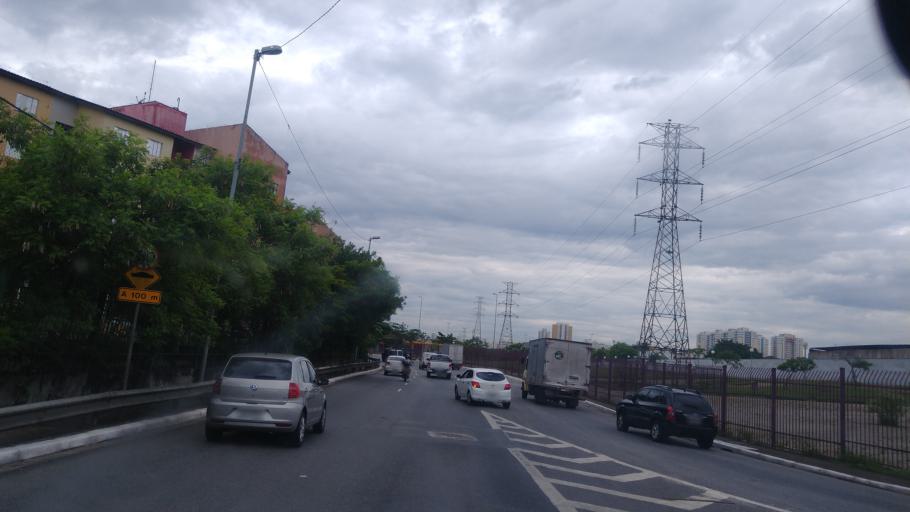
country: BR
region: Sao Paulo
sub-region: Guarulhos
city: Guarulhos
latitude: -23.5181
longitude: -46.5595
